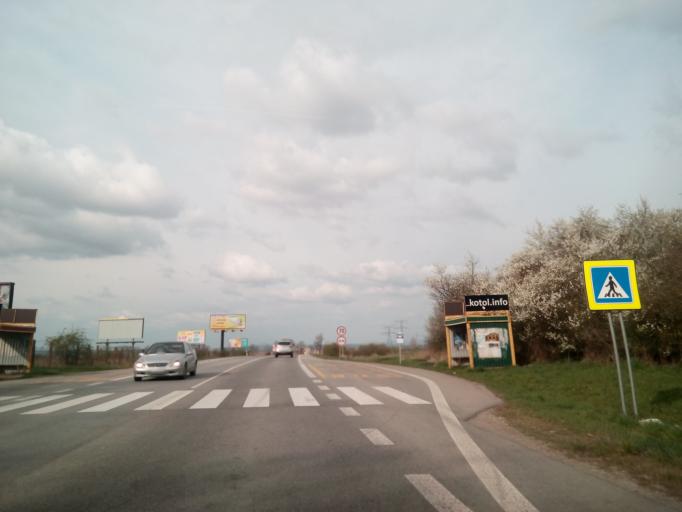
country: SK
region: Kosicky
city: Moldava nad Bodvou
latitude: 48.6072
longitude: 21.1117
